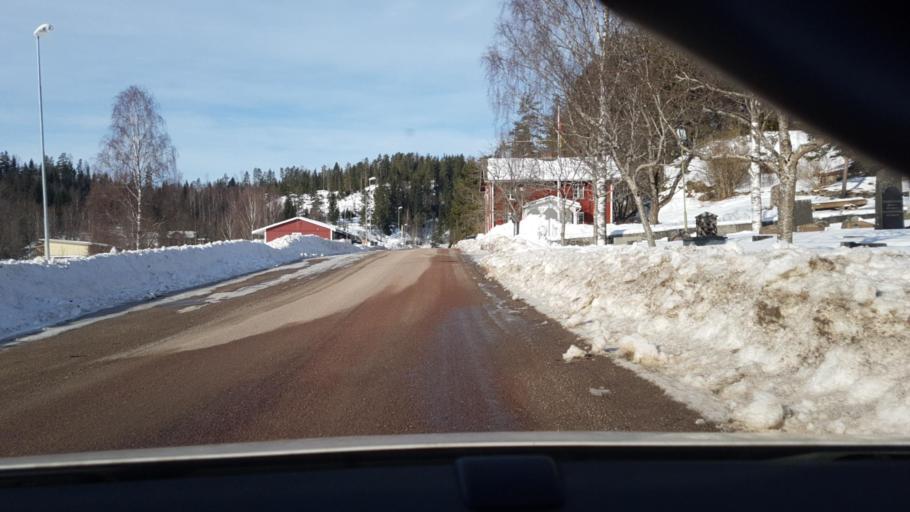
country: NO
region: Hedmark
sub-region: Eidskog
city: Skotterud
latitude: 59.8176
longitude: 12.0146
